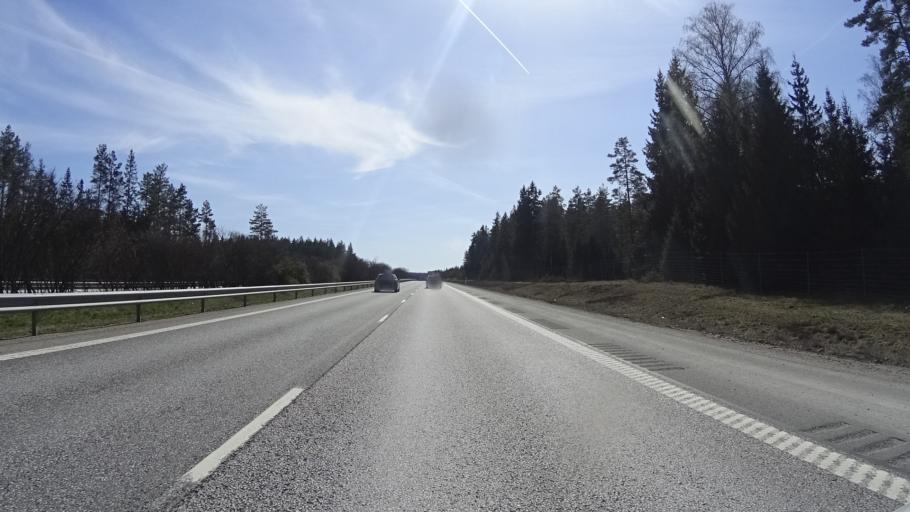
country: SE
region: Joenkoeping
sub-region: Jonkopings Kommun
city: Odensjo
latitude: 57.6188
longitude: 14.1784
